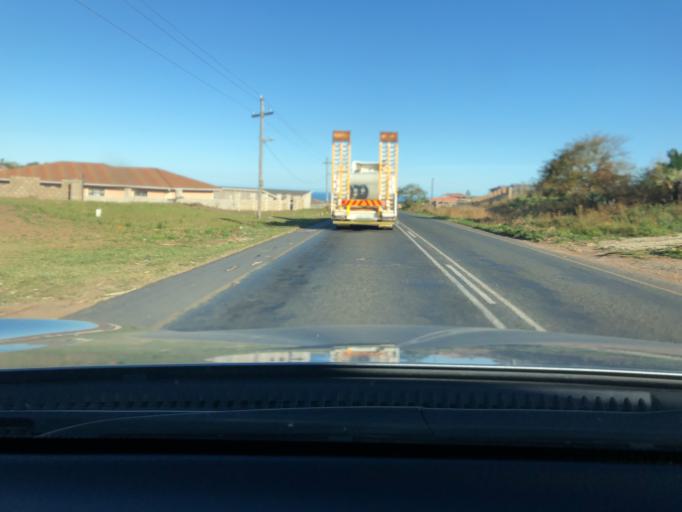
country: ZA
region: KwaZulu-Natal
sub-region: eThekwini Metropolitan Municipality
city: Umkomaas
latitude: -30.0097
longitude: 30.8045
